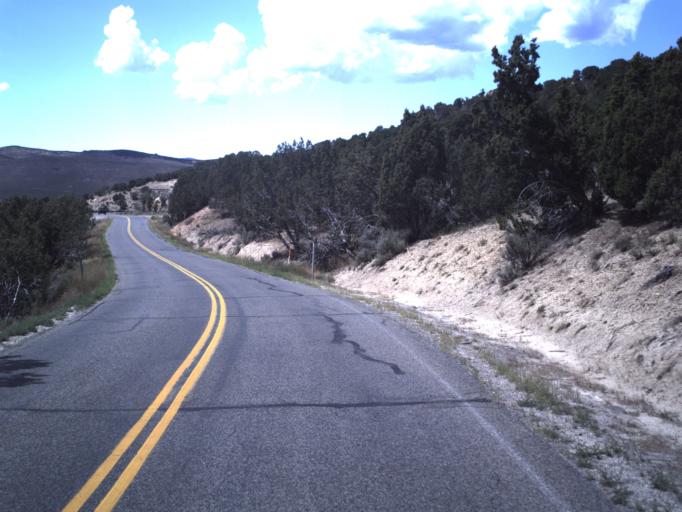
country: US
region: Utah
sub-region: Summit County
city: Oakley
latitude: 40.7626
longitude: -111.3788
